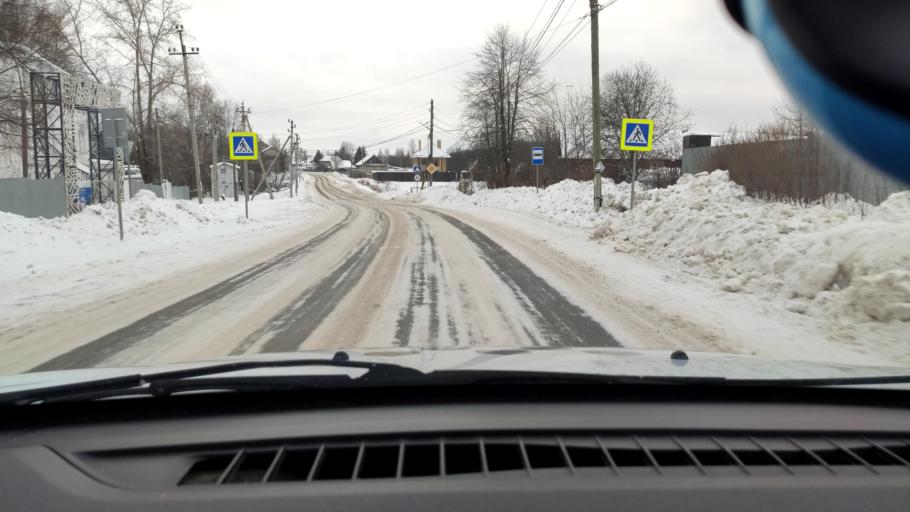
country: RU
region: Perm
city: Overyata
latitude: 58.0779
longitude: 55.9683
